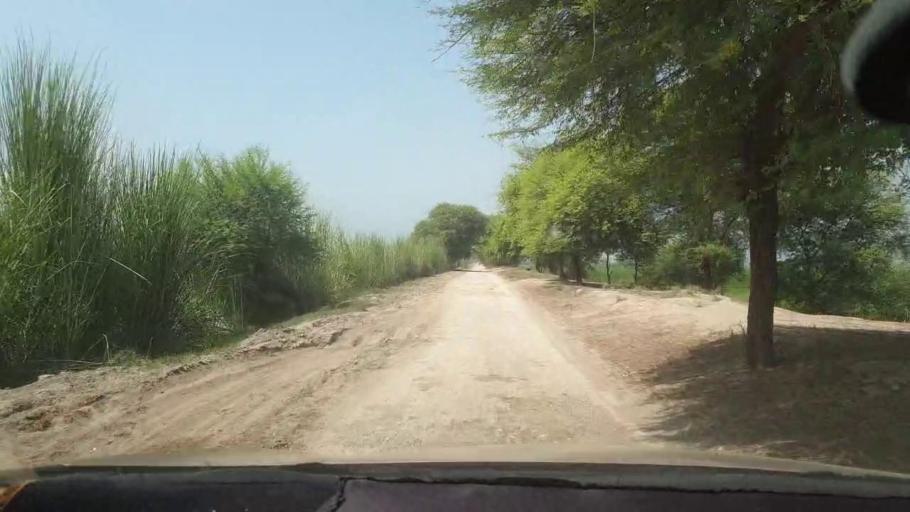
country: PK
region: Sindh
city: Shahdadkot
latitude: 27.7101
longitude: 67.9283
